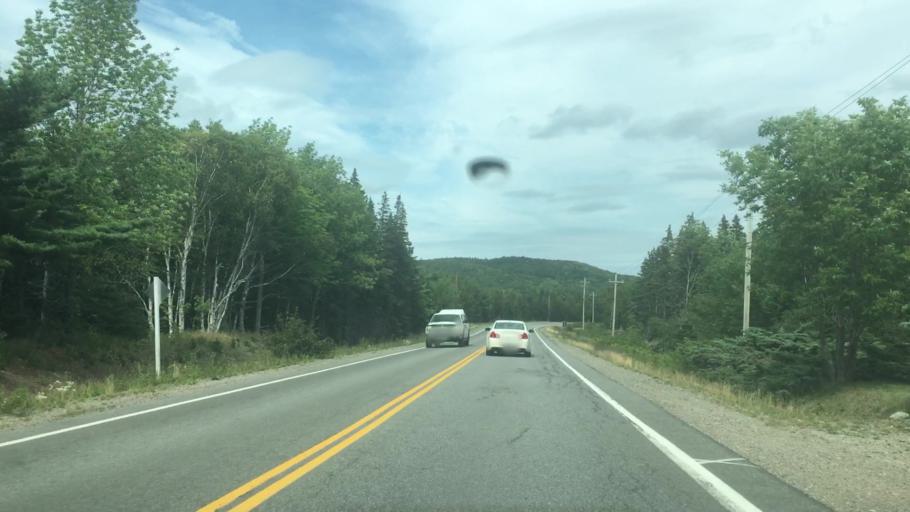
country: CA
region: Nova Scotia
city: Sydney Mines
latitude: 46.5094
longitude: -60.4313
